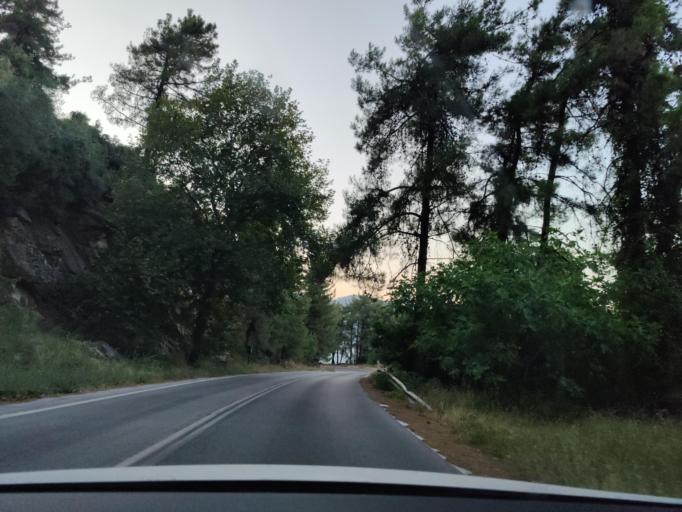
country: GR
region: East Macedonia and Thrace
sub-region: Nomos Kavalas
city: Potamia
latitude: 40.7064
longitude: 24.7668
